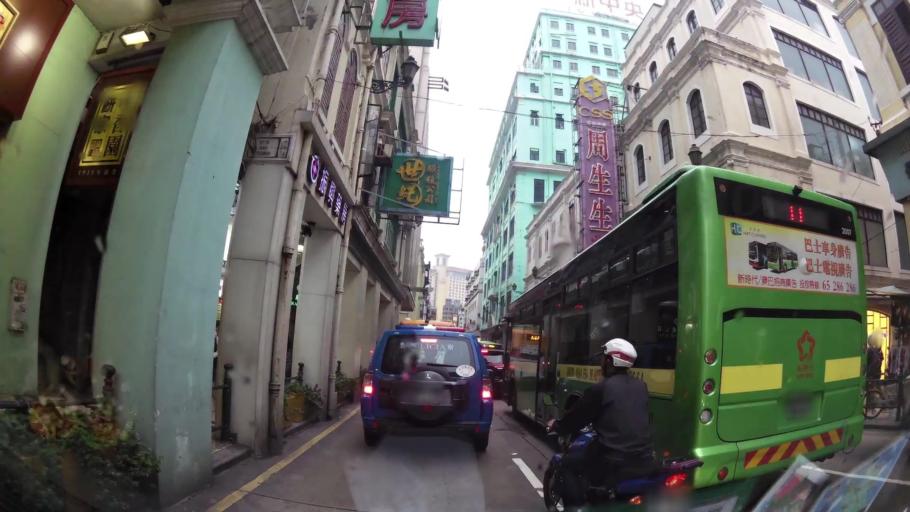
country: MO
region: Macau
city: Macau
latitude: 22.1936
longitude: 113.5394
